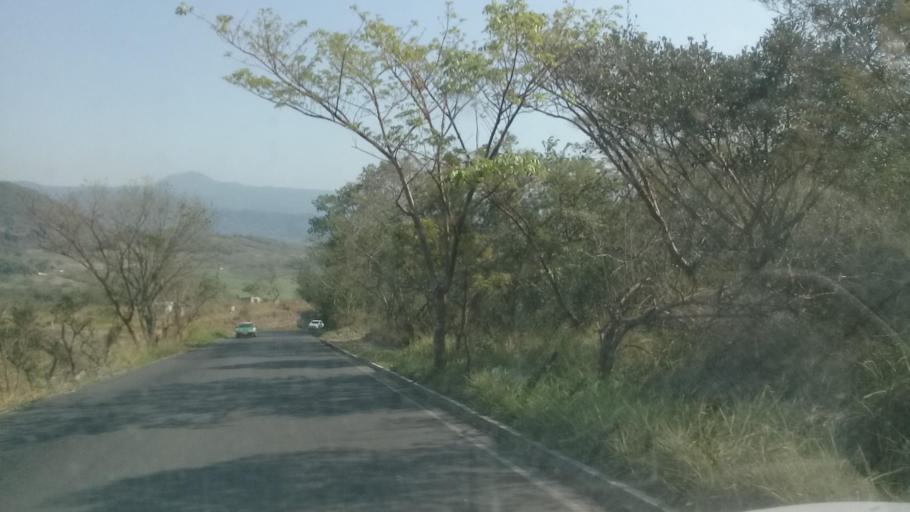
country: MX
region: Veracruz
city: El Castillo
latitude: 19.5745
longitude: -96.8323
